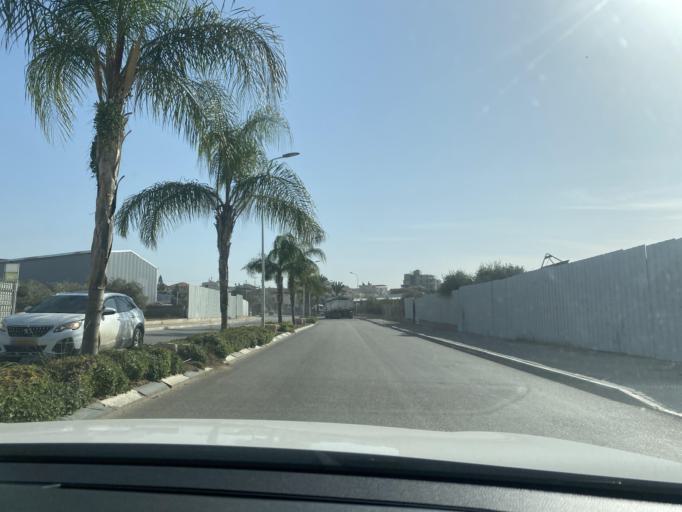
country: IL
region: Central District
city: Jaljulya
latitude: 32.1337
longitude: 34.9637
